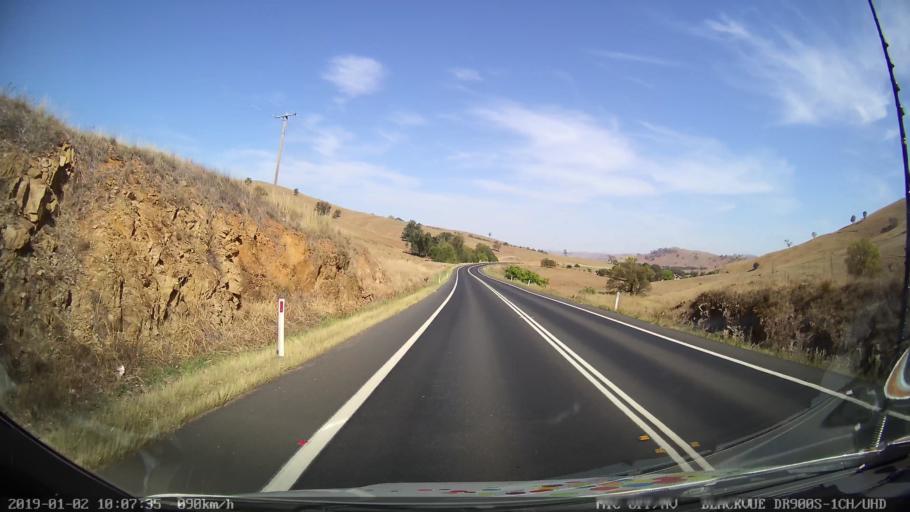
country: AU
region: New South Wales
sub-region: Gundagai
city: Gundagai
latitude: -35.1368
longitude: 148.1109
